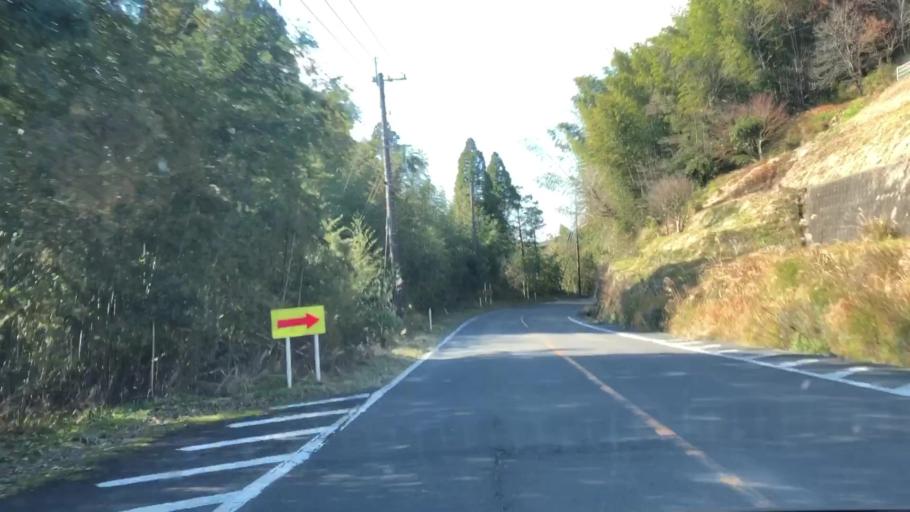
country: JP
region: Kagoshima
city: Satsumasendai
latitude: 31.8596
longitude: 130.4048
